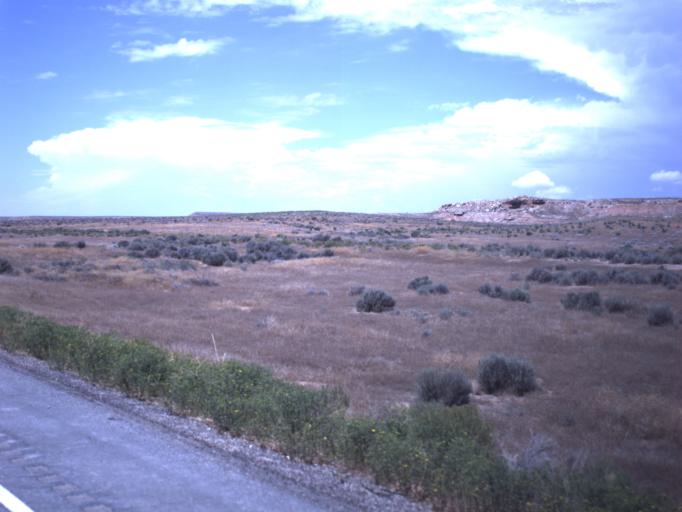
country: US
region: Utah
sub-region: Uintah County
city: Maeser
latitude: 40.3295
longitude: -109.6639
